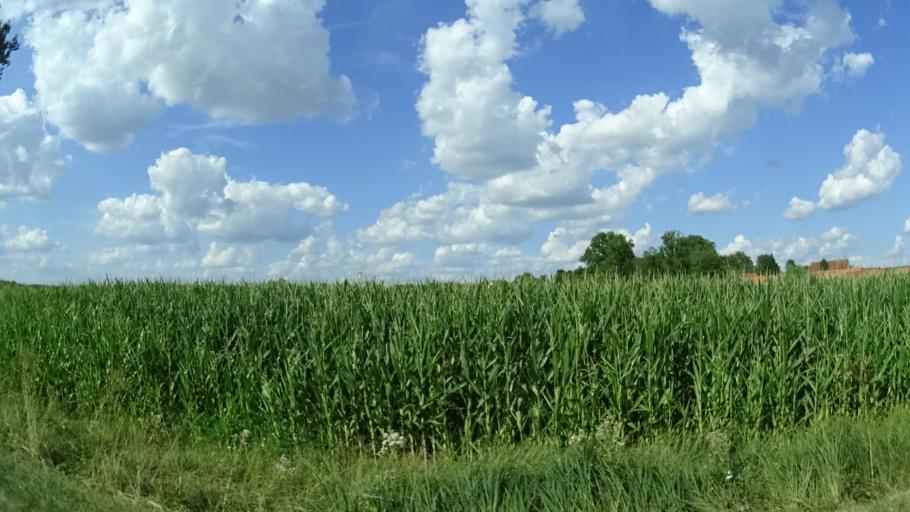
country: DE
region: Bavaria
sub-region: Regierungsbezirk Unterfranken
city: Bundorf
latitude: 50.2668
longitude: 10.5340
